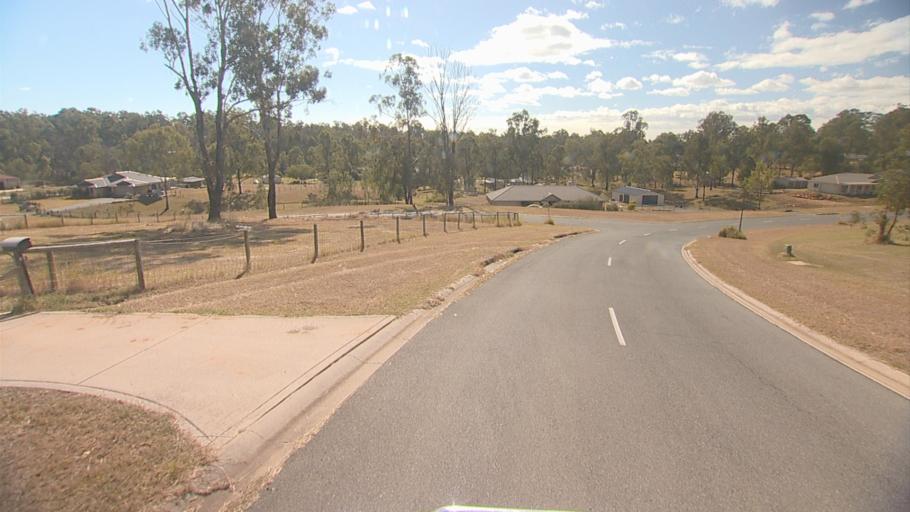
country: AU
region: Queensland
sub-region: Logan
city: Cedar Vale
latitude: -27.8883
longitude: 153.0033
